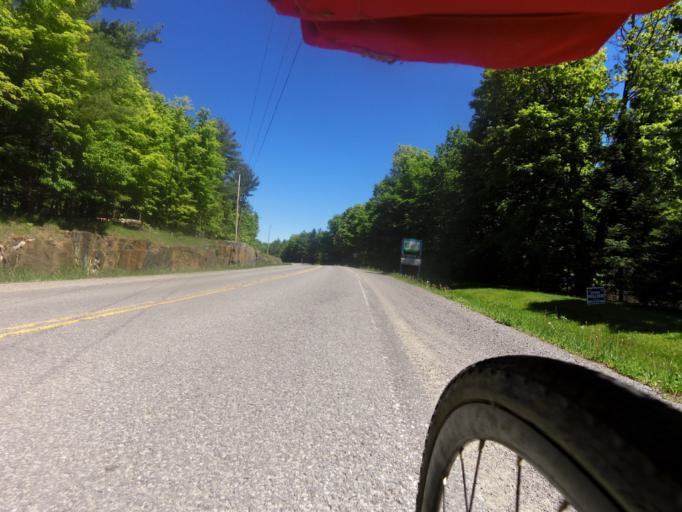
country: CA
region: Ontario
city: Carleton Place
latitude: 45.1856
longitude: -76.3429
